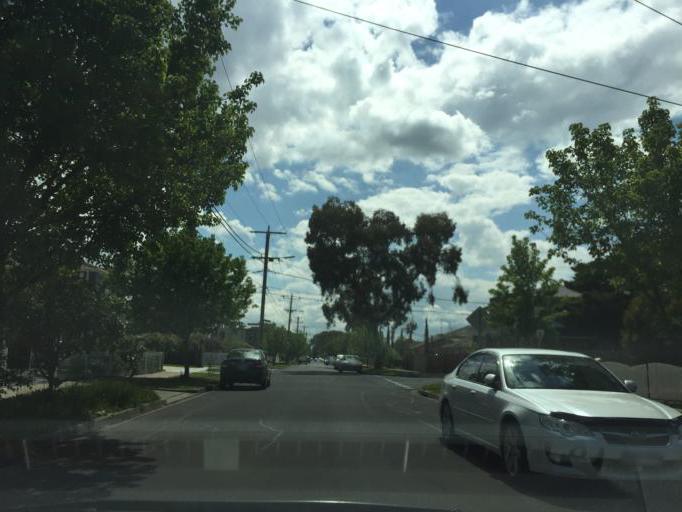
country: AU
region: Victoria
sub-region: Maribyrnong
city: Maidstone
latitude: -37.7896
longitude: 144.8712
